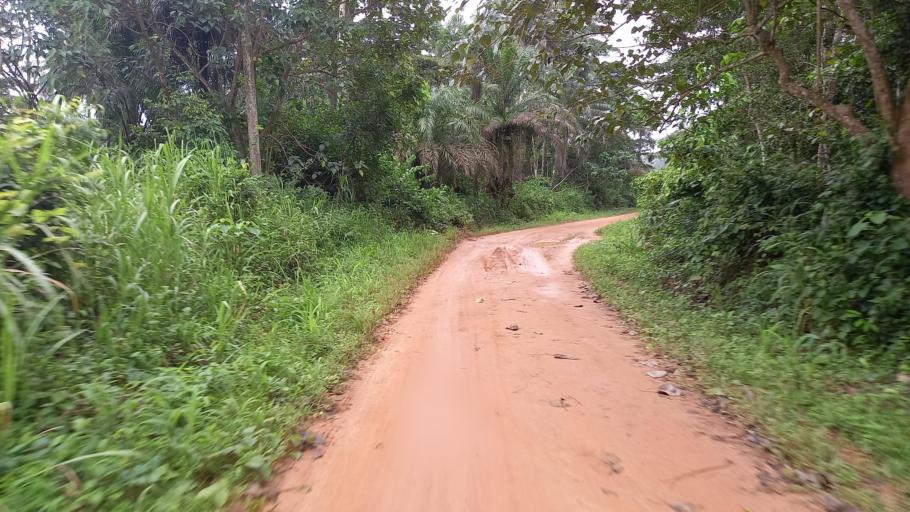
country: SL
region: Eastern Province
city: Kailahun
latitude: 8.2414
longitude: -10.5184
